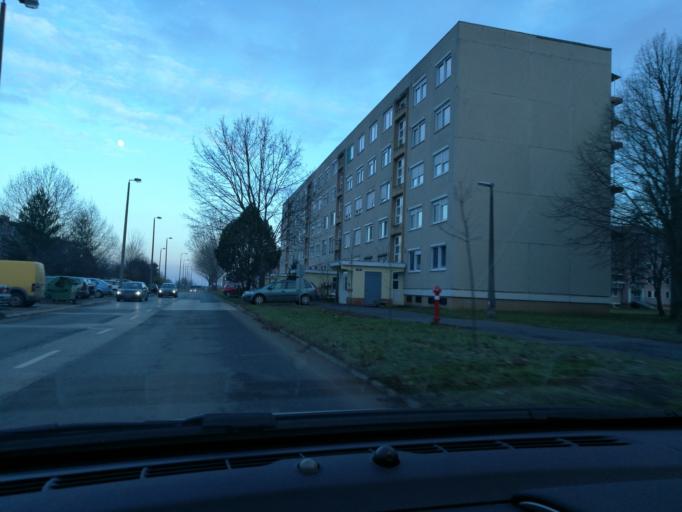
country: HU
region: Szabolcs-Szatmar-Bereg
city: Nyiregyhaza
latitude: 47.9620
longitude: 21.7389
